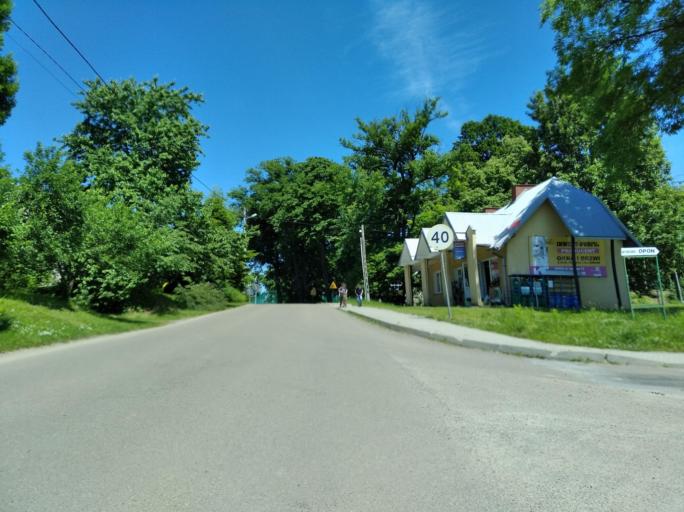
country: PL
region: Subcarpathian Voivodeship
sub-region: Powiat jasielski
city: Tarnowiec
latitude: 49.7298
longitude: 21.5765
